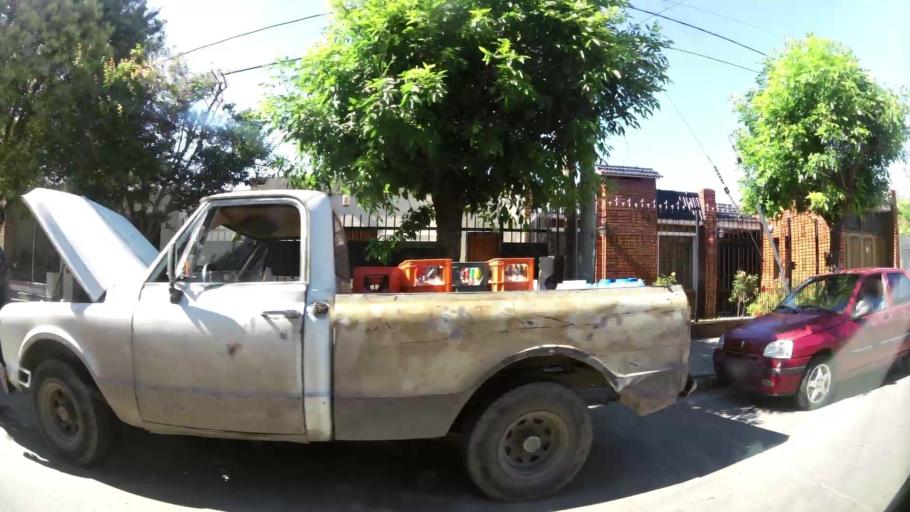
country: AR
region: Cordoba
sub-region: Departamento de Capital
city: Cordoba
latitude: -31.4343
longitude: -64.1483
